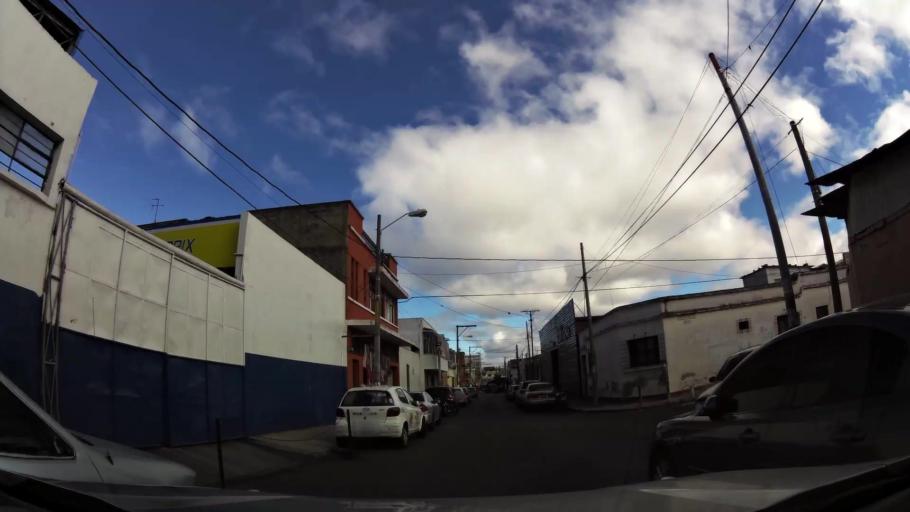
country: GT
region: Guatemala
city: Guatemala City
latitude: 14.6202
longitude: -90.5093
